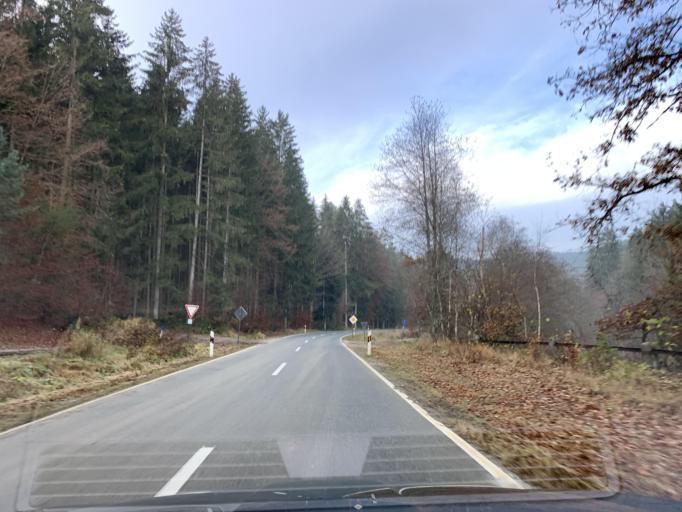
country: DE
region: Bavaria
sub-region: Upper Palatinate
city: Thanstein
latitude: 49.3692
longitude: 12.4298
